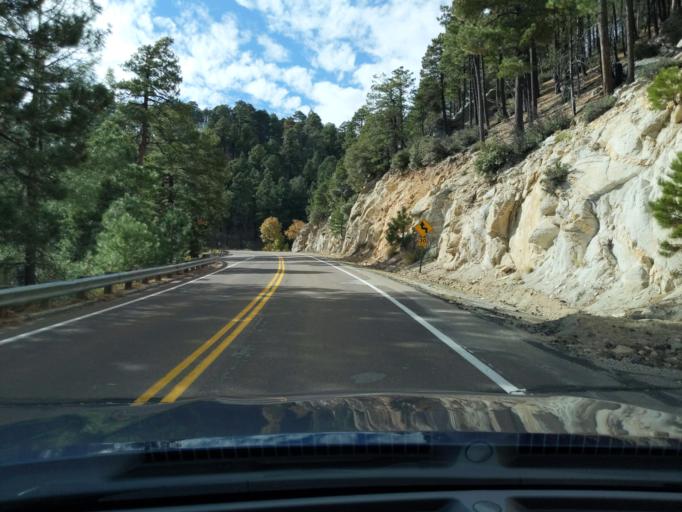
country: US
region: Arizona
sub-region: Pima County
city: Tanque Verde
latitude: 32.4110
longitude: -110.7214
